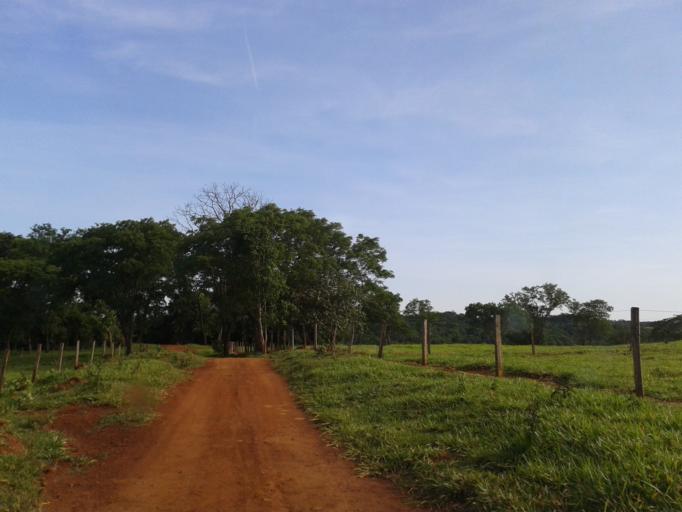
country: BR
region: Minas Gerais
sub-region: Centralina
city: Centralina
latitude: -18.7111
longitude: -49.1951
